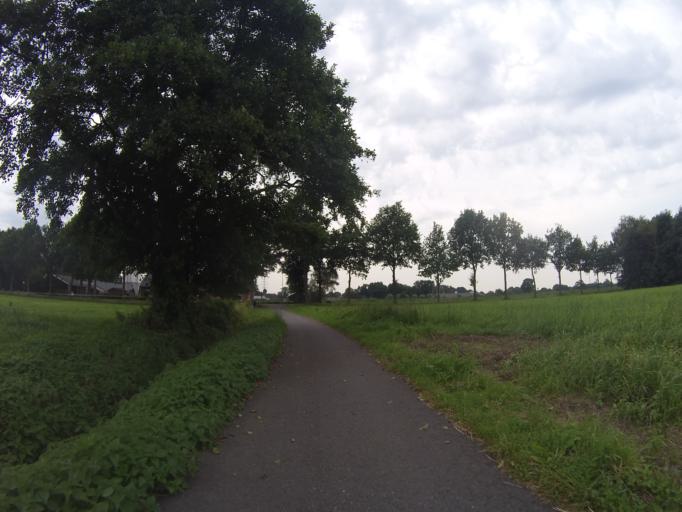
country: NL
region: Gelderland
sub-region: Gemeente Putten
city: Putten
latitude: 52.2334
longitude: 5.5916
